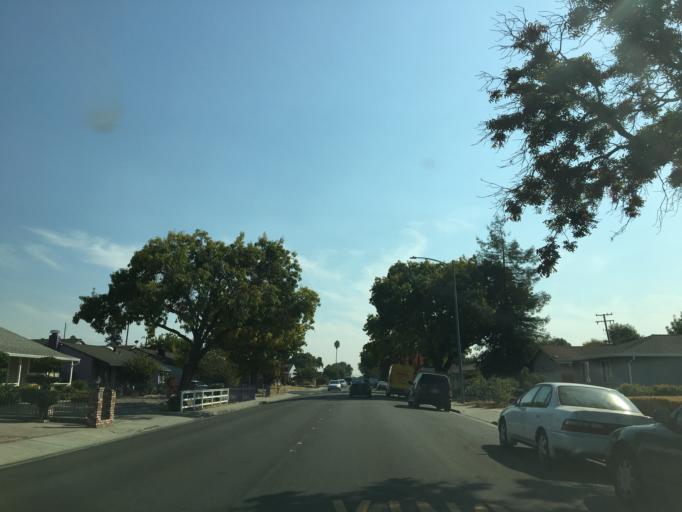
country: US
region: California
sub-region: Santa Clara County
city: Milpitas
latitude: 37.4576
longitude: -121.9082
